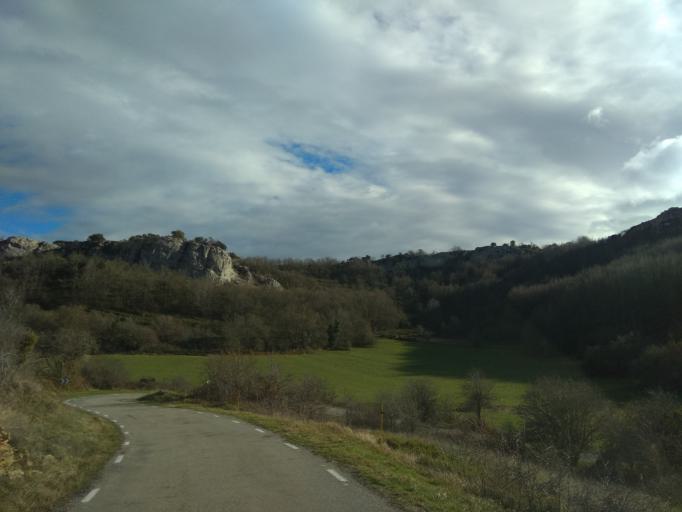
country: ES
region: Cantabria
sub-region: Provincia de Cantabria
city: San Martin de Elines
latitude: 42.9529
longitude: -3.8078
